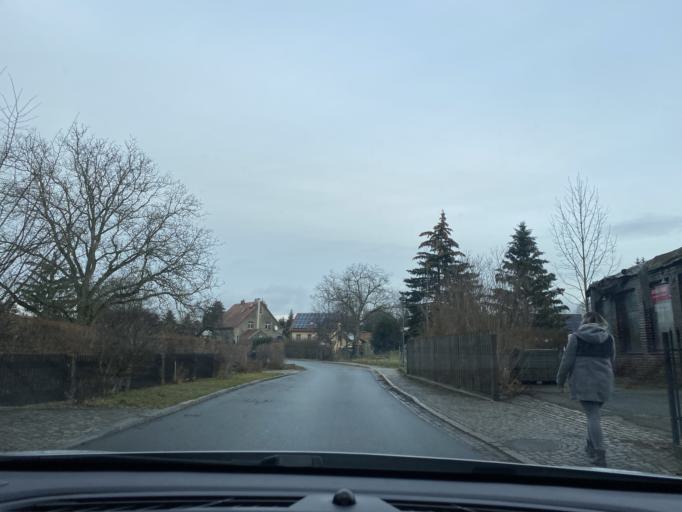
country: DE
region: Saxony
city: Reichenbach
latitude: 51.1415
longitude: 14.8042
